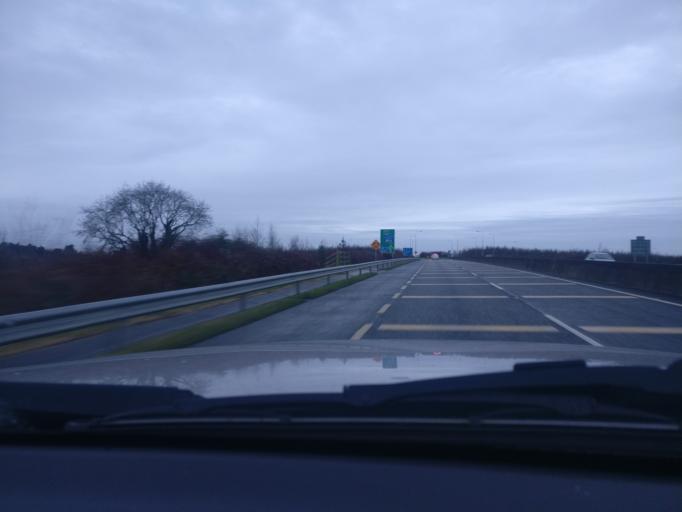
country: IE
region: Leinster
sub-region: An Mhi
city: Navan
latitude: 53.6413
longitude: -6.7362
